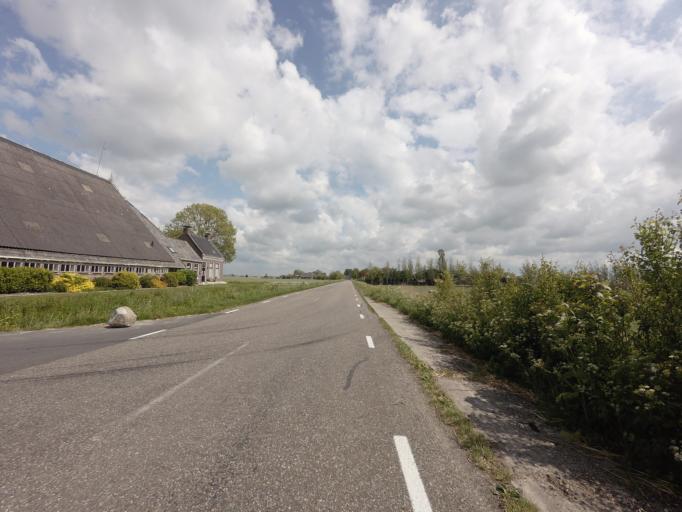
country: NL
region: Friesland
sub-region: Gemeente Littenseradiel
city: Makkum
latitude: 53.0975
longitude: 5.6529
